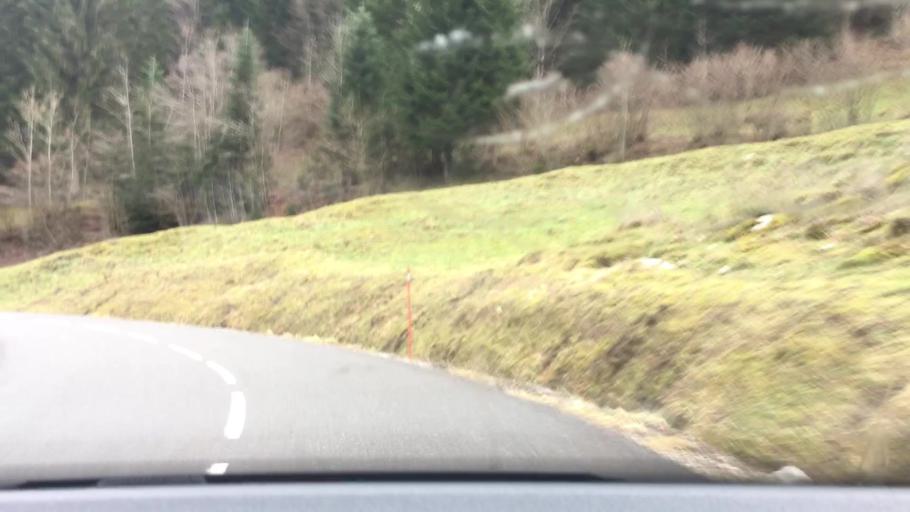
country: FR
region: Rhone-Alpes
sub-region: Departement de la Haute-Savoie
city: Abondance
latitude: 46.2868
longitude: 6.6670
